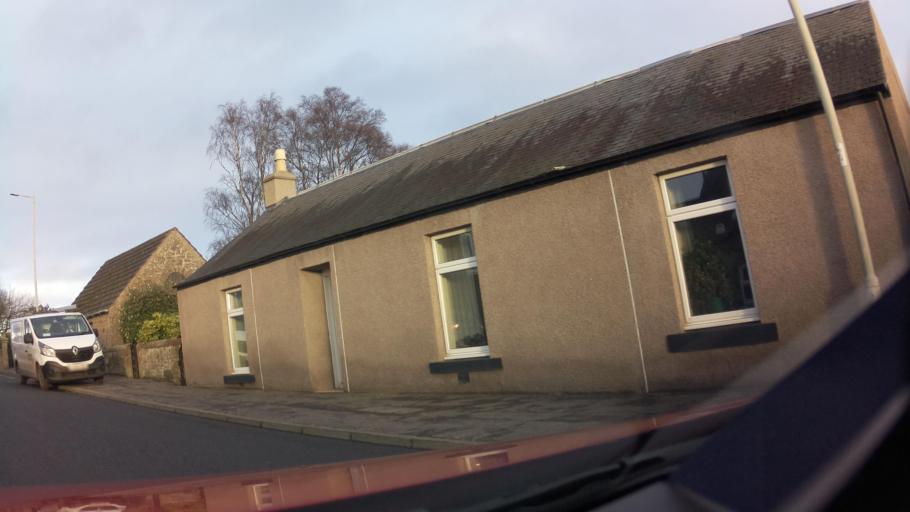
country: GB
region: Scotland
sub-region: Fife
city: Tayport
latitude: 56.5135
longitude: -2.8173
